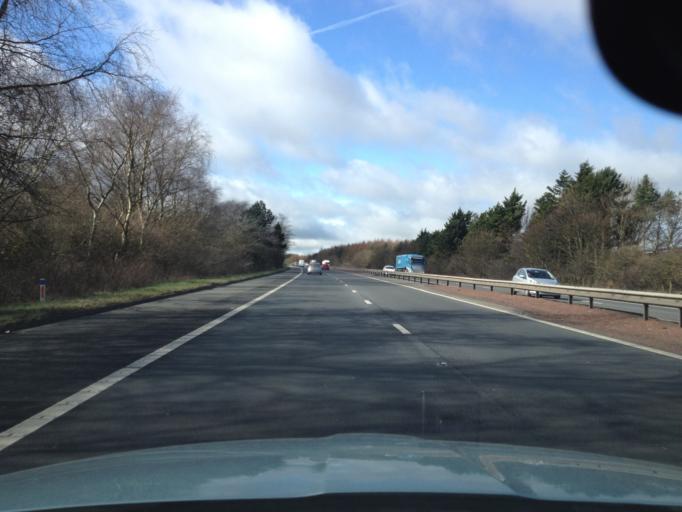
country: GB
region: Scotland
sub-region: West Lothian
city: Broxburn
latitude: 55.9201
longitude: -3.4948
